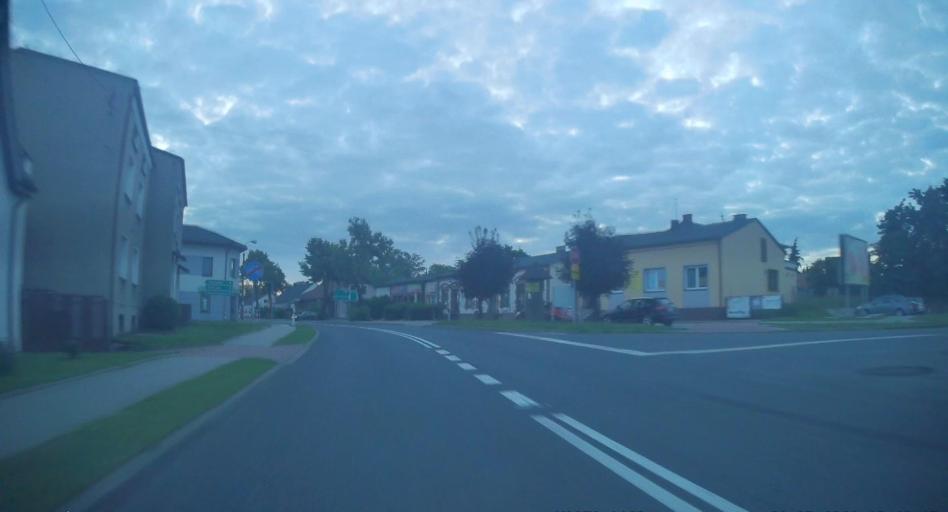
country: PL
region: Opole Voivodeship
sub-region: Powiat oleski
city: Dalachow
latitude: 51.0379
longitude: 18.6020
